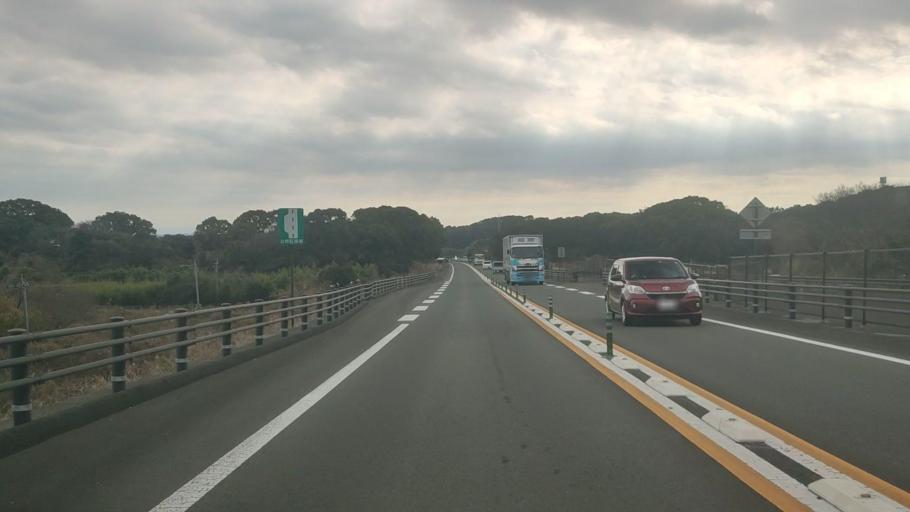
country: JP
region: Nagasaki
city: Shimabara
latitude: 32.7675
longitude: 130.3593
